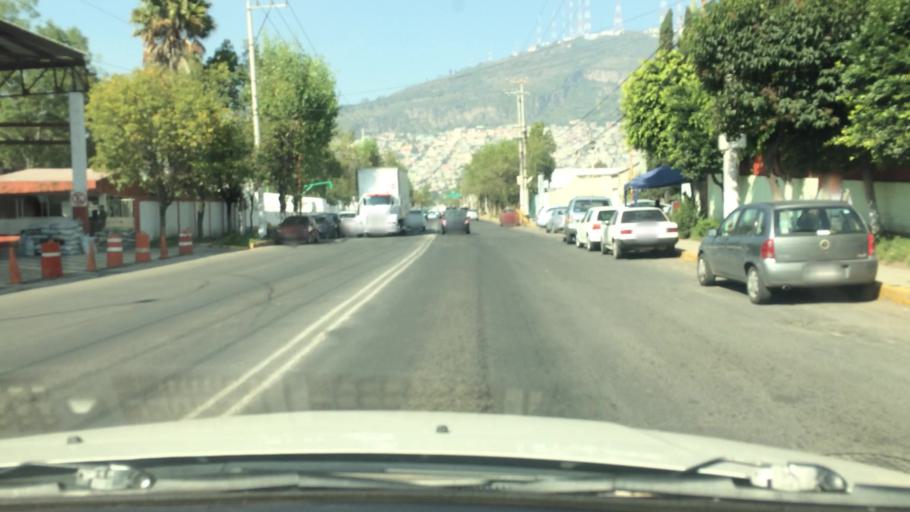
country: MX
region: Mexico
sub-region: Tlalnepantla de Baz
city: Puerto Escondido (Tepeolulco Puerto Escondido)
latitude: 19.5259
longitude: -99.1096
